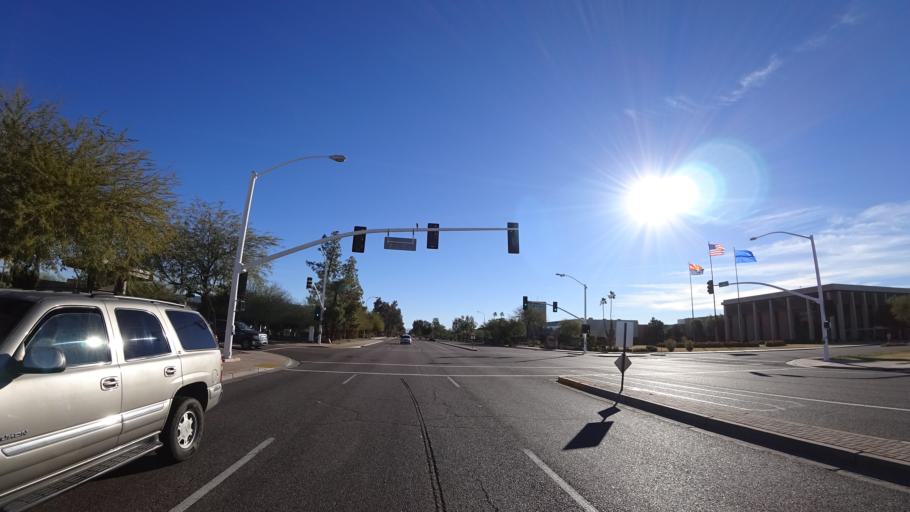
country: US
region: Arizona
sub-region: Maricopa County
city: Scottsdale
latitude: 33.4659
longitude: -111.9049
